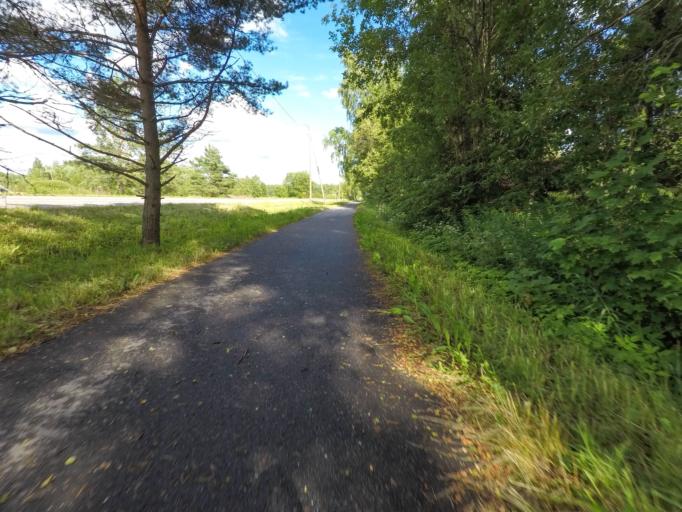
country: FI
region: South Karelia
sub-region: Lappeenranta
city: Joutseno
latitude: 61.1281
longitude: 28.5003
